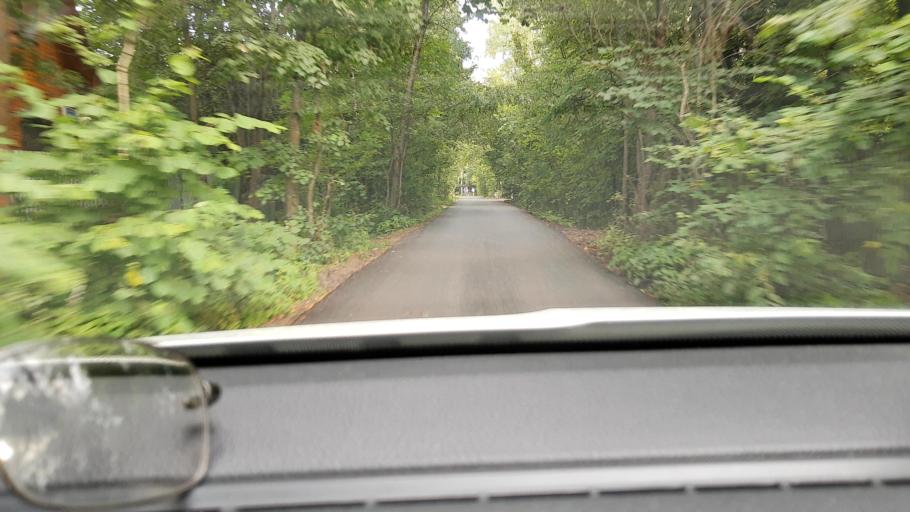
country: RU
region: Moskovskaya
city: Kokoshkino
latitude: 55.5942
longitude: 37.1623
